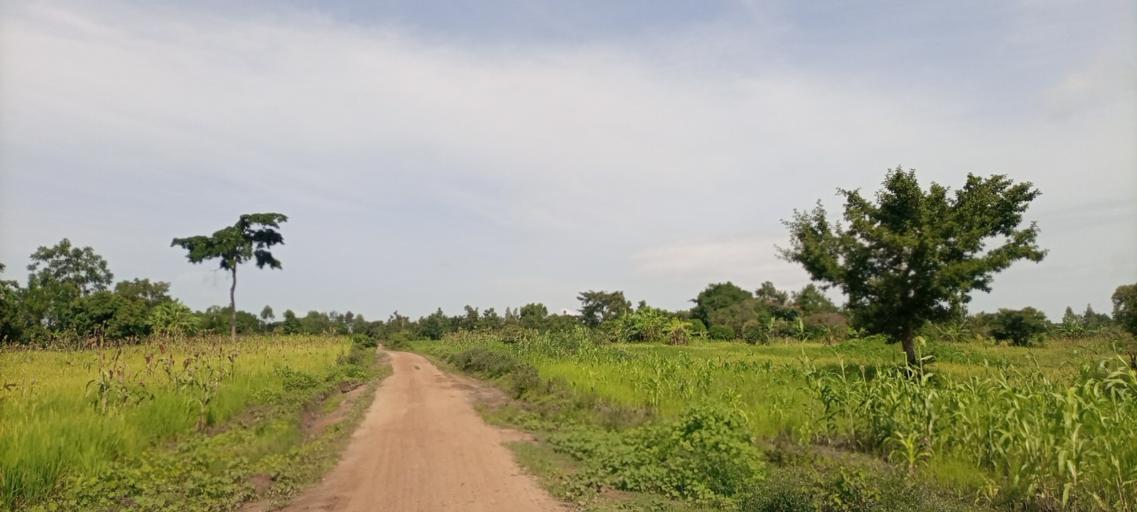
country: UG
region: Eastern Region
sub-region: Mbale District
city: Mbale
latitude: 1.1277
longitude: 34.0338
